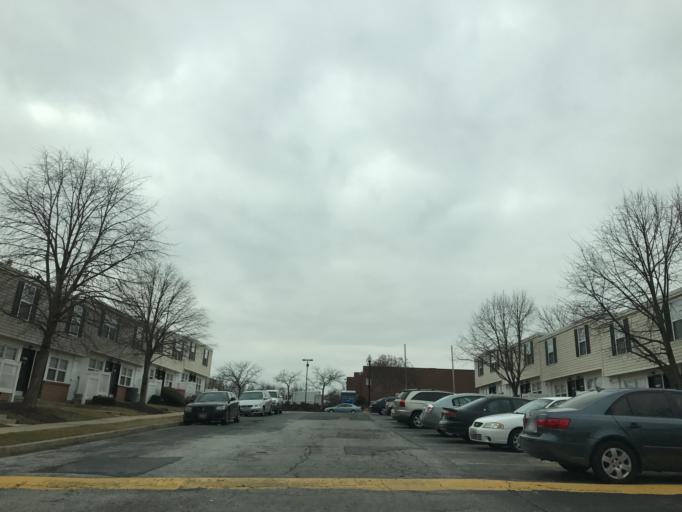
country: US
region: Maryland
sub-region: Baltimore County
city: Rossville
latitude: 39.3406
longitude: -76.4900
